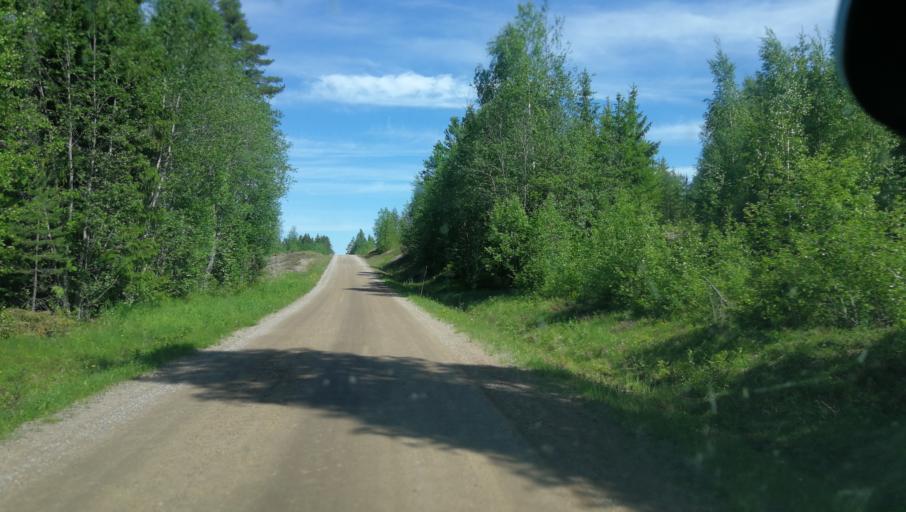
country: SE
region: Dalarna
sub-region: Vansbro Kommun
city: Vansbro
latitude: 60.8229
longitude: 14.1943
